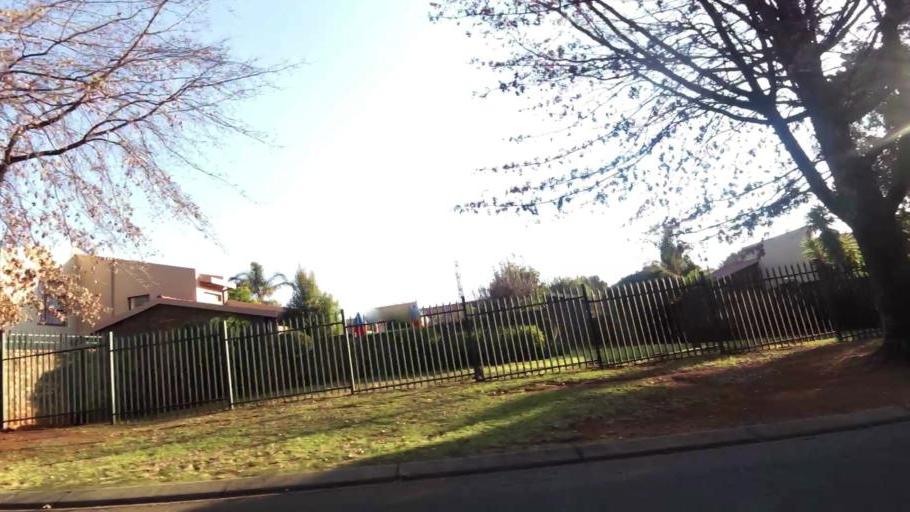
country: ZA
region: Gauteng
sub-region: City of Johannesburg Metropolitan Municipality
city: Johannesburg
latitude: -26.1613
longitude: 27.9811
